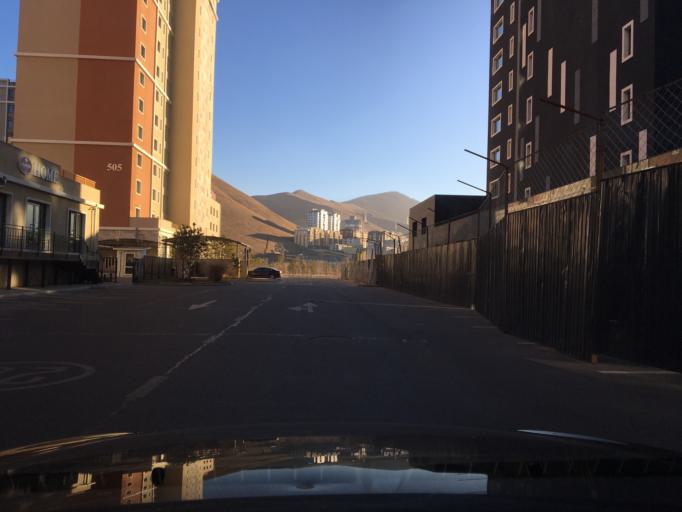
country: MN
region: Ulaanbaatar
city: Ulaanbaatar
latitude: 47.8910
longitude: 106.9237
